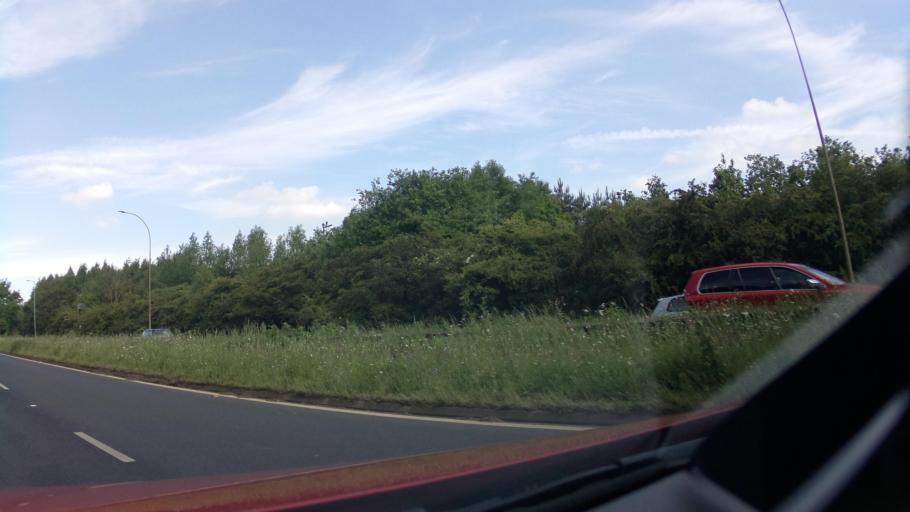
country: GB
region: England
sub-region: North Lincolnshire
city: Manton
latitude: 53.5605
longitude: -0.5970
